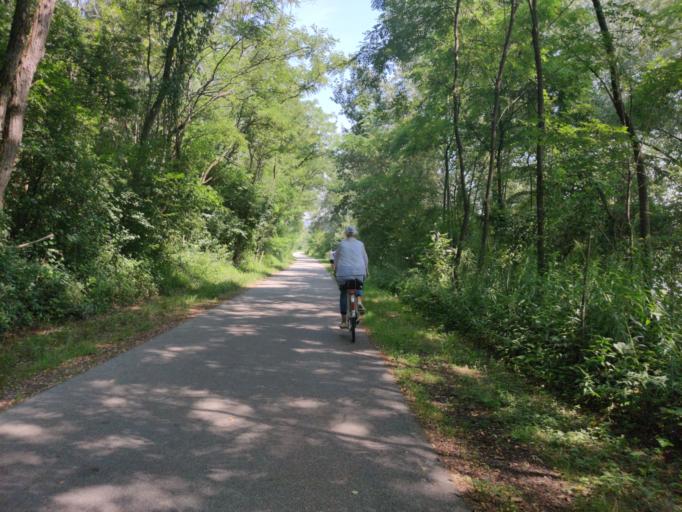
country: AT
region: Upper Austria
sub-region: Politischer Bezirk Urfahr-Umgebung
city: Ottensheim
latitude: 48.3244
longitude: 14.1517
